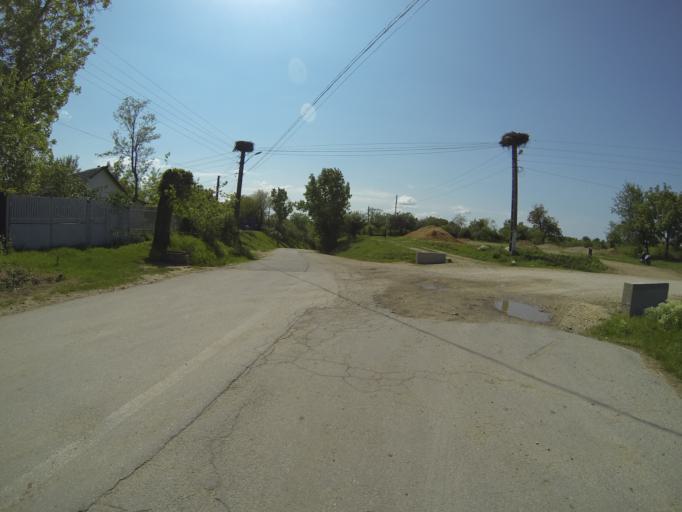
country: RO
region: Dolj
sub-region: Comuna Orodelu
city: Orodelu
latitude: 44.2501
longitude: 23.2356
